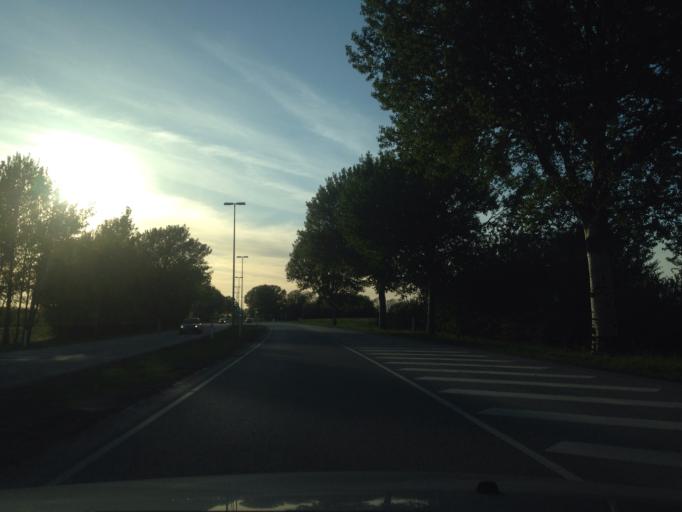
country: DK
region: Zealand
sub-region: Greve Kommune
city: Greve
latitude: 55.5886
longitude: 12.2496
